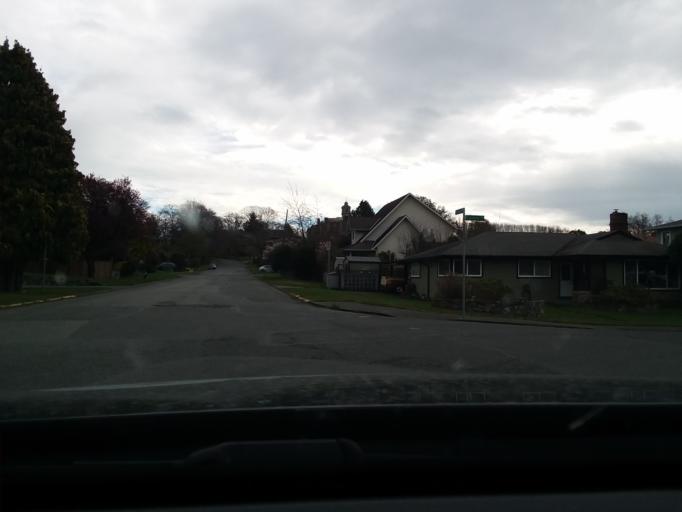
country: CA
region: British Columbia
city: Oak Bay
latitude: 48.4481
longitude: -123.3296
